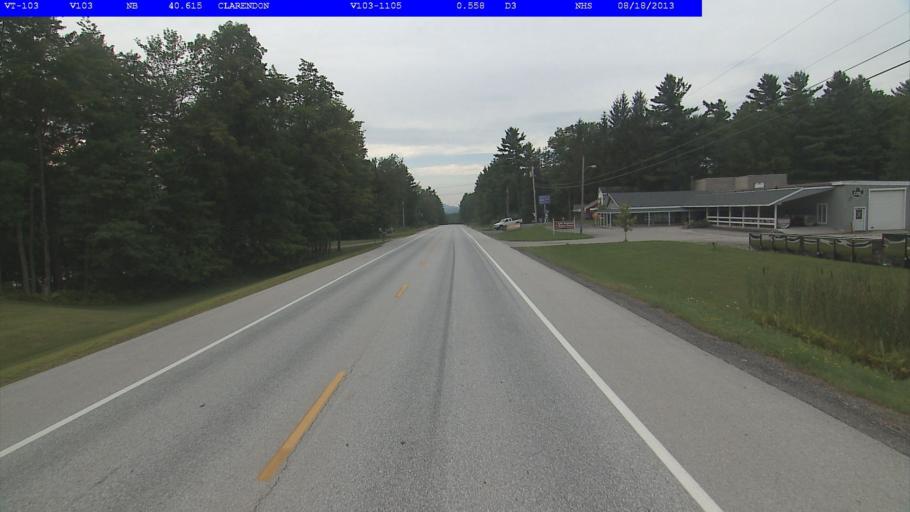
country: US
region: Vermont
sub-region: Rutland County
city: Rutland
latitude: 43.5305
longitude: -72.9370
